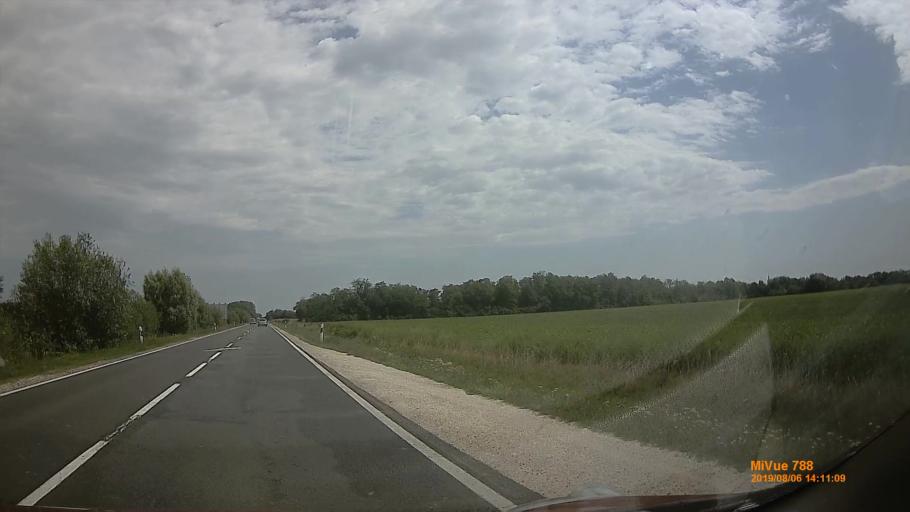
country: HU
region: Vas
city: Szombathely
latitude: 47.2193
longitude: 16.6601
